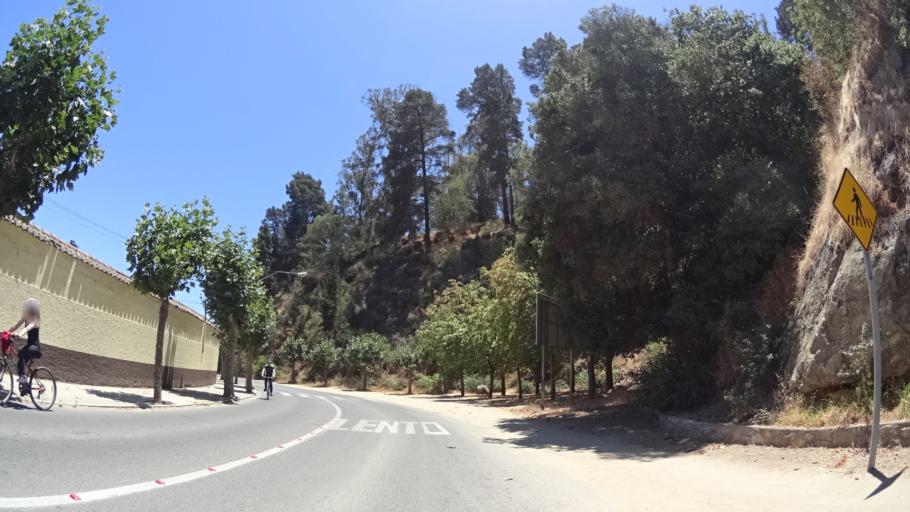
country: CL
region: Valparaiso
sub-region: Provincia de Valparaiso
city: Vina del Mar
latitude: -33.0199
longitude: -71.5377
